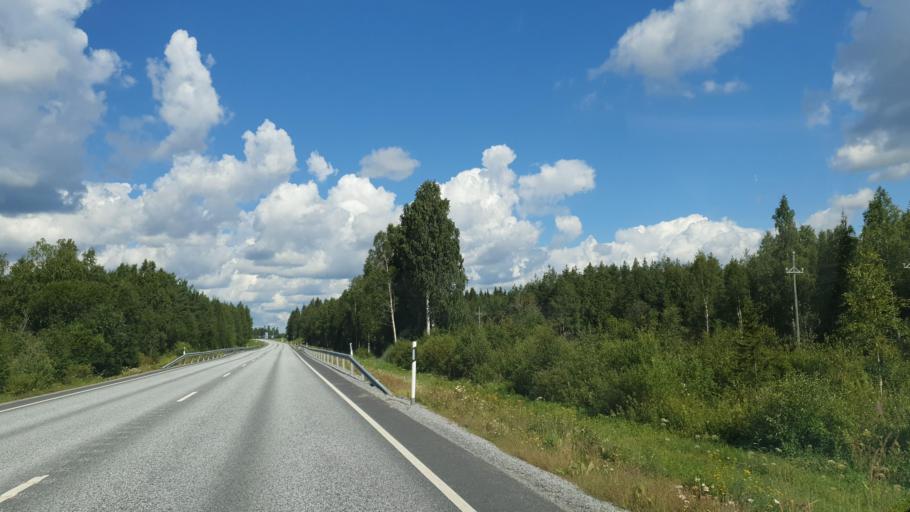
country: FI
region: Northern Savo
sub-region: Ylae-Savo
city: Sonkajaervi
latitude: 63.8576
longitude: 27.4414
